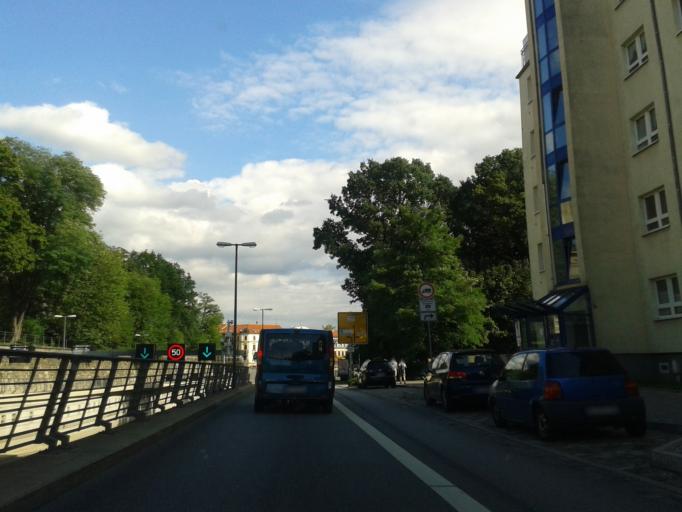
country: DE
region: Saxony
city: Albertstadt
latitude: 51.0708
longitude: 13.7728
